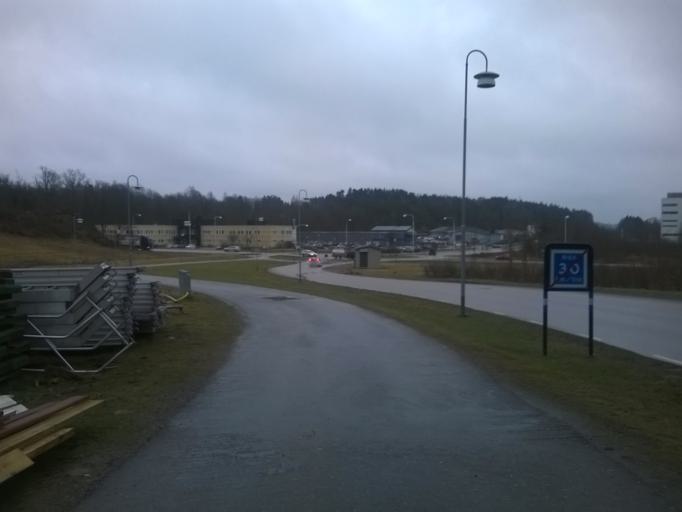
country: SE
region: Vaestra Goetaland
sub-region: Kungalvs Kommun
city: Kungalv
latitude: 57.8905
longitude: 11.9487
